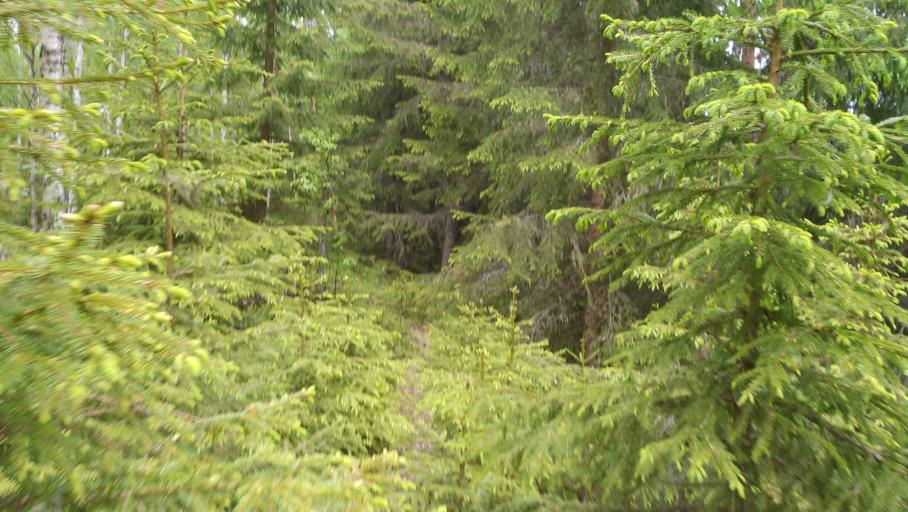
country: SE
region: Vaesterbotten
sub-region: Vannas Kommun
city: Vannasby
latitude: 64.0143
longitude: 19.9078
